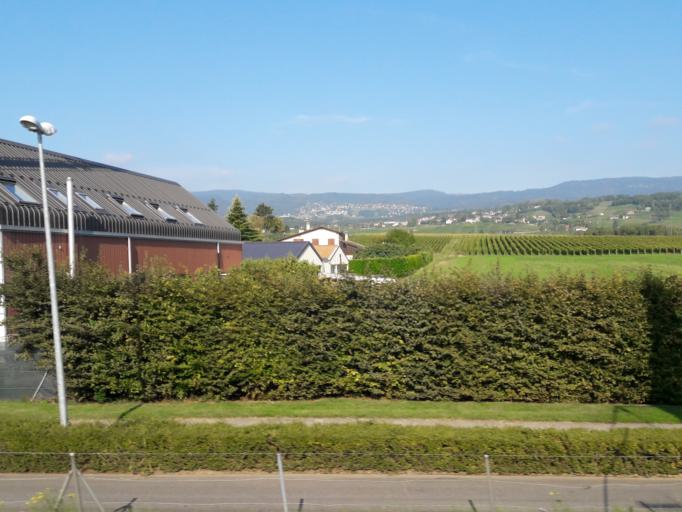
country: CH
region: Vaud
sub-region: Nyon District
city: Gland
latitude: 46.4250
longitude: 6.2744
